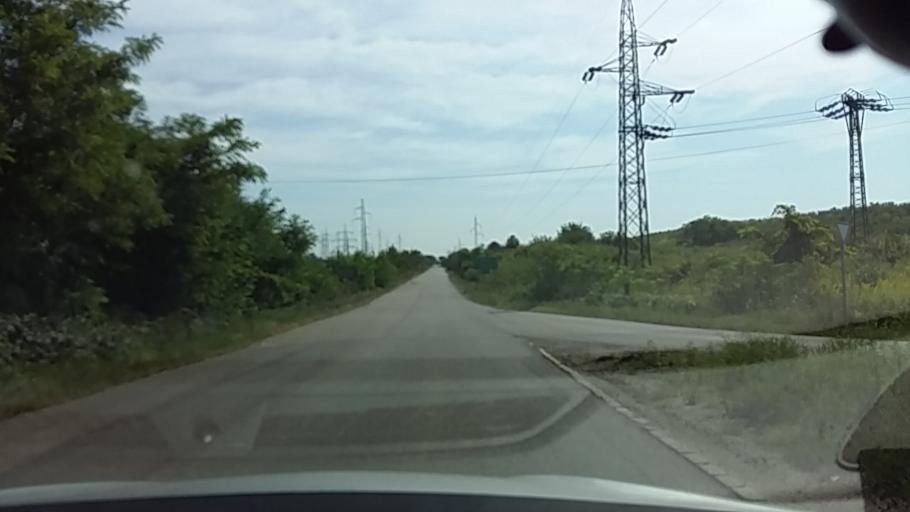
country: HU
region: Heves
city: Domoszlo
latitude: 47.7722
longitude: 20.0975
